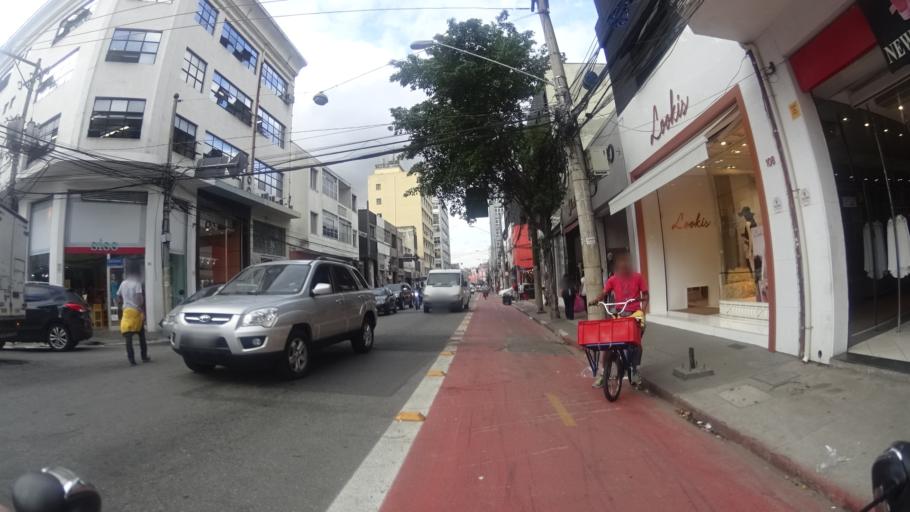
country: BR
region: Sao Paulo
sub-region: Sao Paulo
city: Sao Paulo
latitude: -23.5296
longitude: -46.6412
